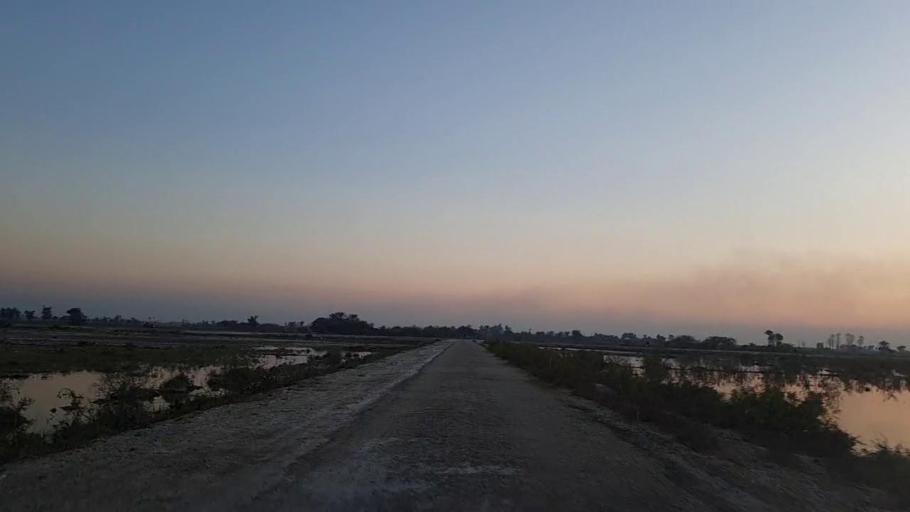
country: PK
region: Sindh
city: Bandhi
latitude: 26.5901
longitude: 68.3359
